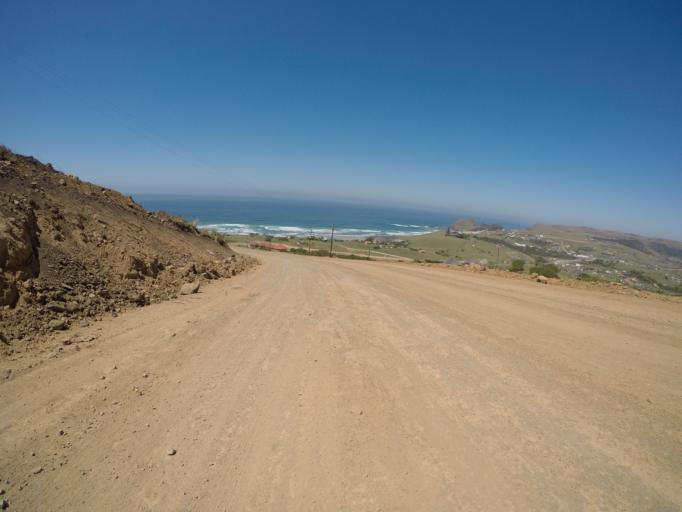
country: ZA
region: Eastern Cape
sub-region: OR Tambo District Municipality
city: Libode
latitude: -32.0247
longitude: 29.1149
